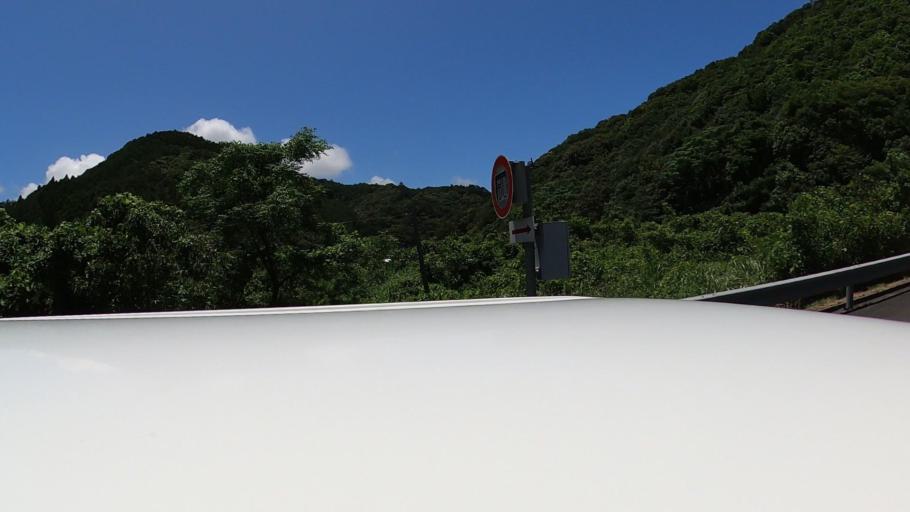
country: JP
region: Miyazaki
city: Nobeoka
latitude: 32.5319
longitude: 131.6642
